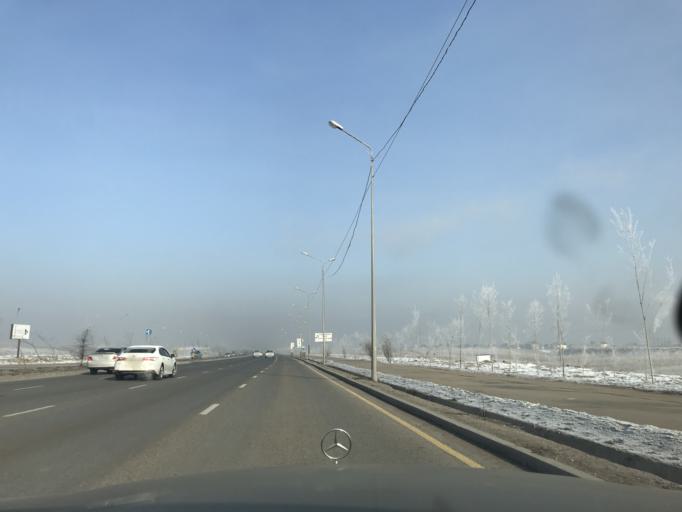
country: KZ
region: Almaty Oblysy
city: Burunday
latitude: 43.3202
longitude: 76.8340
